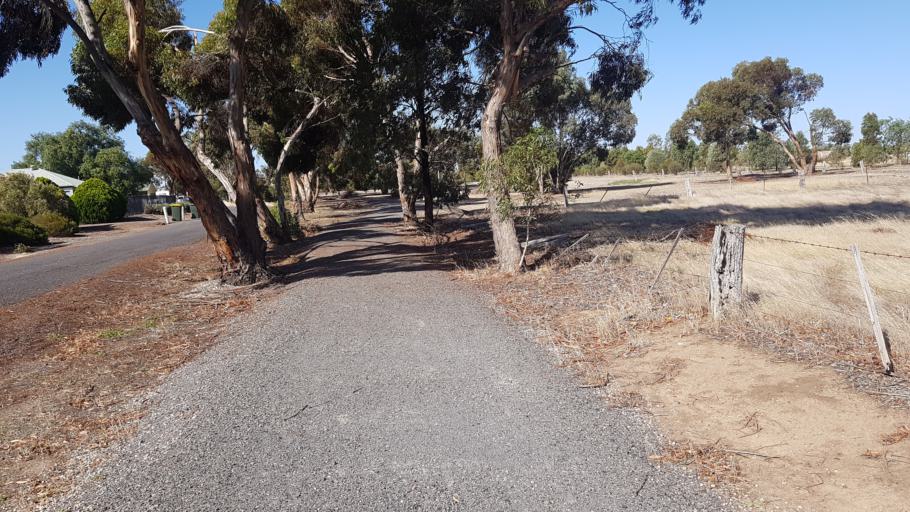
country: AU
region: Victoria
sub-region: Horsham
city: Horsham
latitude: -36.7463
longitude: 141.9374
